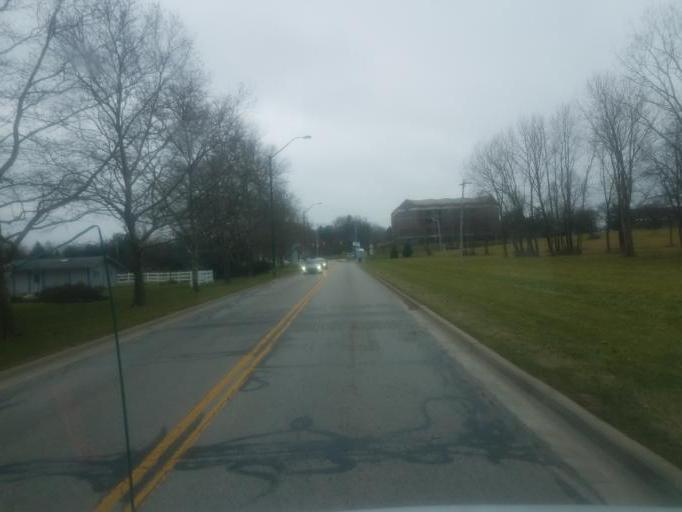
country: US
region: Ohio
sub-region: Franklin County
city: Westerville
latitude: 40.1123
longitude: -82.9428
